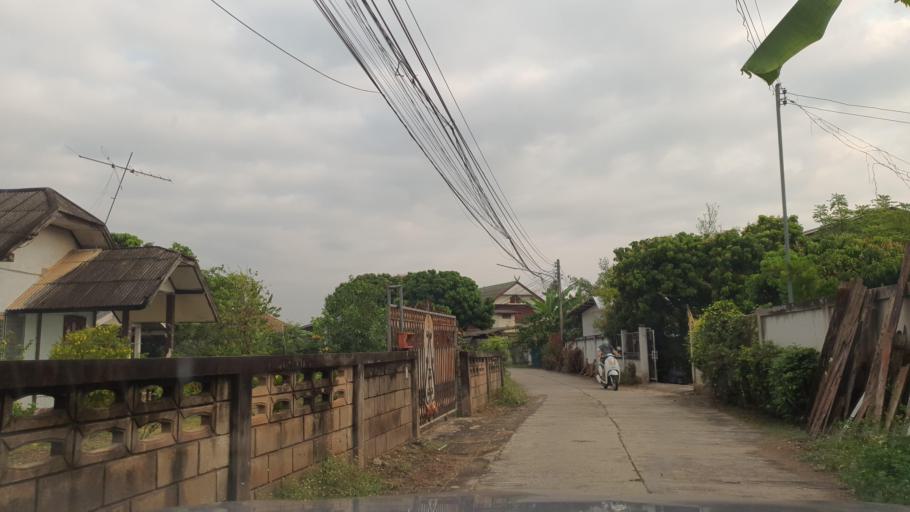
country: TH
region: Chiang Mai
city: Hang Dong
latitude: 18.6940
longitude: 98.9506
